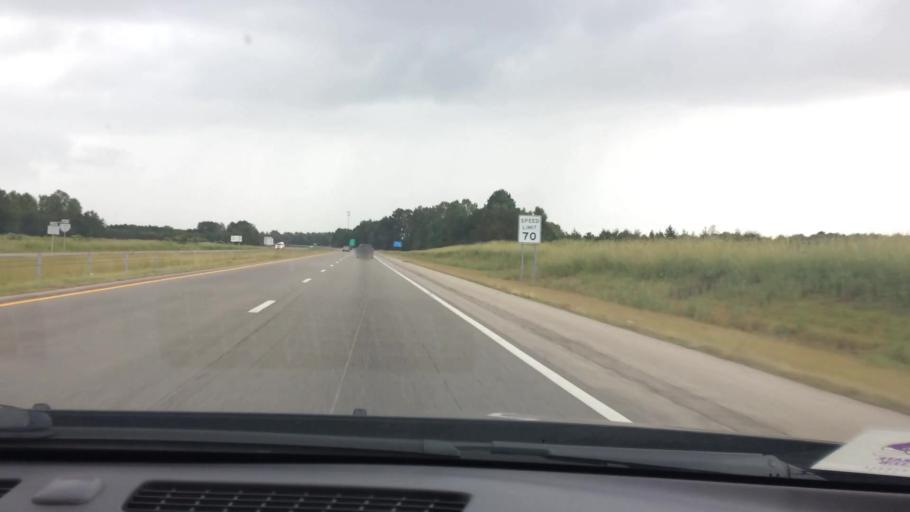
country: US
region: North Carolina
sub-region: Wilson County
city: Lucama
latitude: 35.7200
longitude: -78.0058
